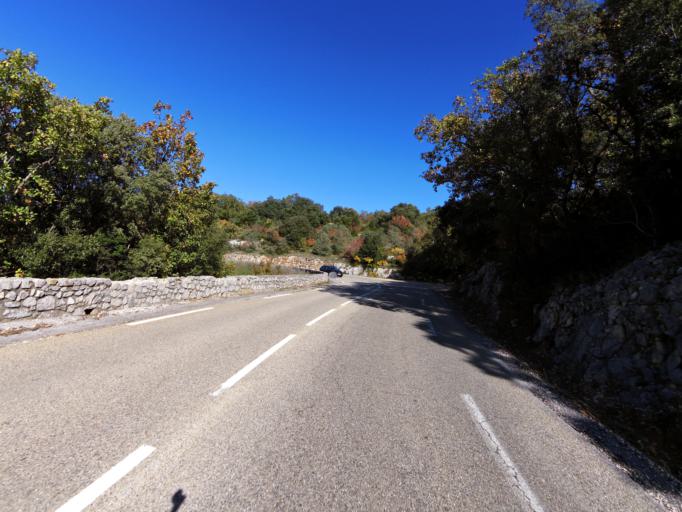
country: FR
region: Rhone-Alpes
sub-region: Departement de l'Ardeche
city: Ruoms
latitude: 44.4023
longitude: 4.4184
